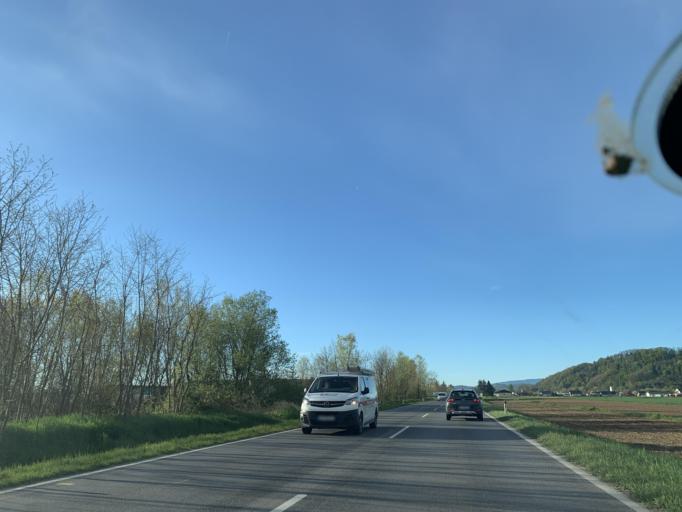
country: AT
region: Styria
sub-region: Politischer Bezirk Leibnitz
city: Kaindorf an der Sulm
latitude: 46.8166
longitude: 15.5256
